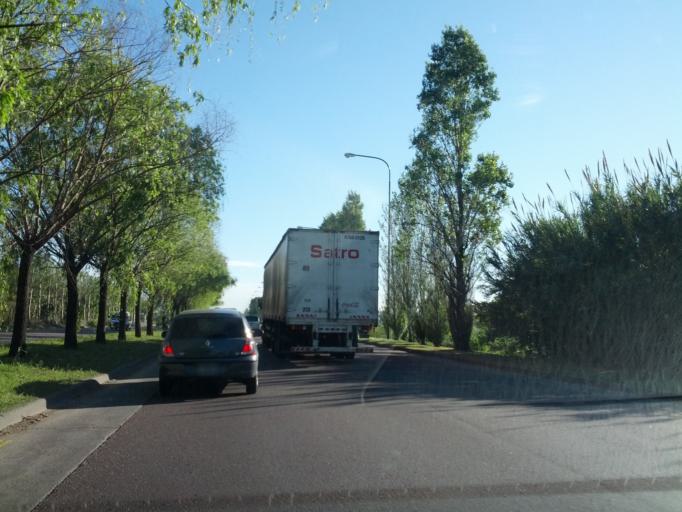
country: AR
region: Buenos Aires F.D.
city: Villa Lugano
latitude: -34.6860
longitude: -58.4454
